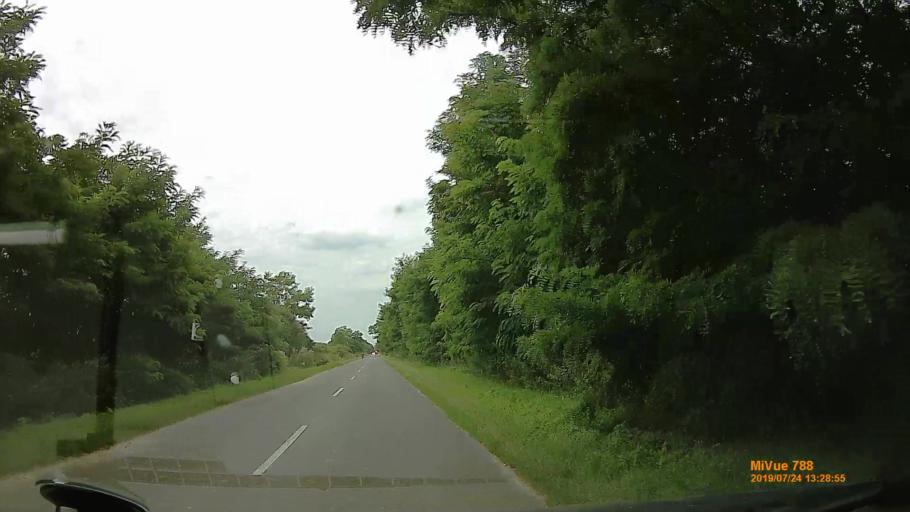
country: UA
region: Zakarpattia
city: Batiovo
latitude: 48.2245
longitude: 22.4088
